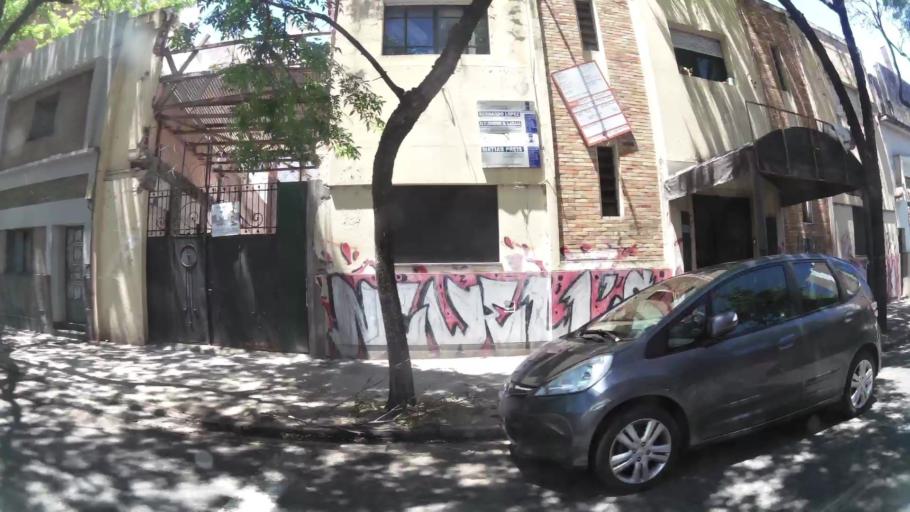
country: AR
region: Santa Fe
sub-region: Departamento de Rosario
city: Rosario
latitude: -32.9475
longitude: -60.6557
